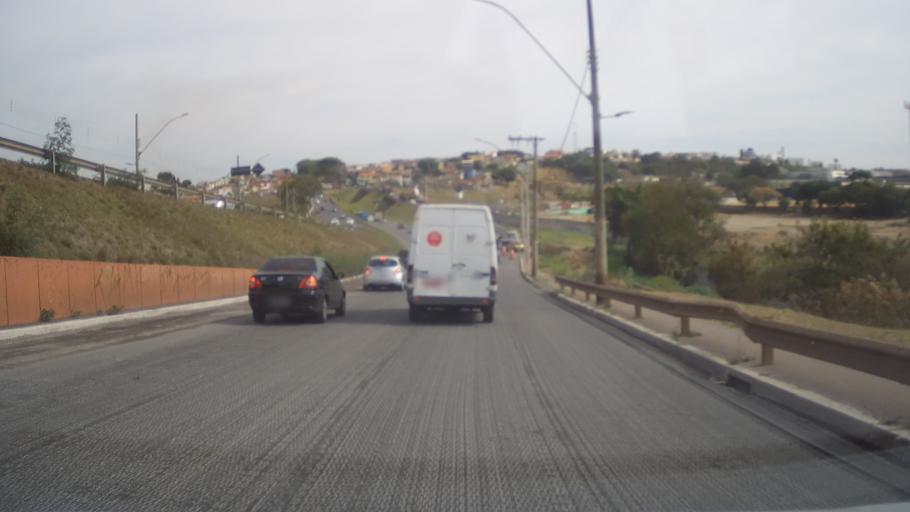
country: BR
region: Minas Gerais
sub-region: Contagem
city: Contagem
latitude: -19.9412
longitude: -44.0264
